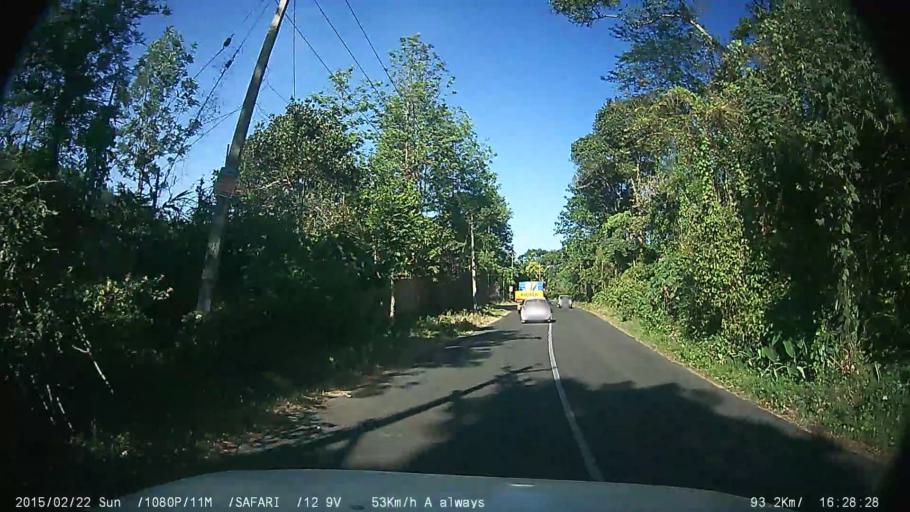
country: IN
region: Tamil Nadu
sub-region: Theni
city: Gudalur
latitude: 9.6106
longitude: 77.1472
